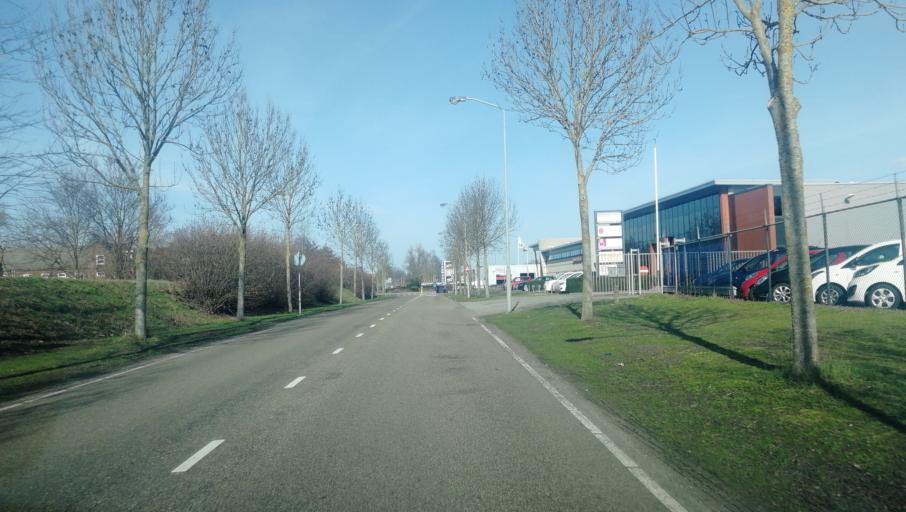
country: NL
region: Limburg
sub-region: Gemeente Venlo
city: Venlo
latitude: 51.3551
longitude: 6.1754
